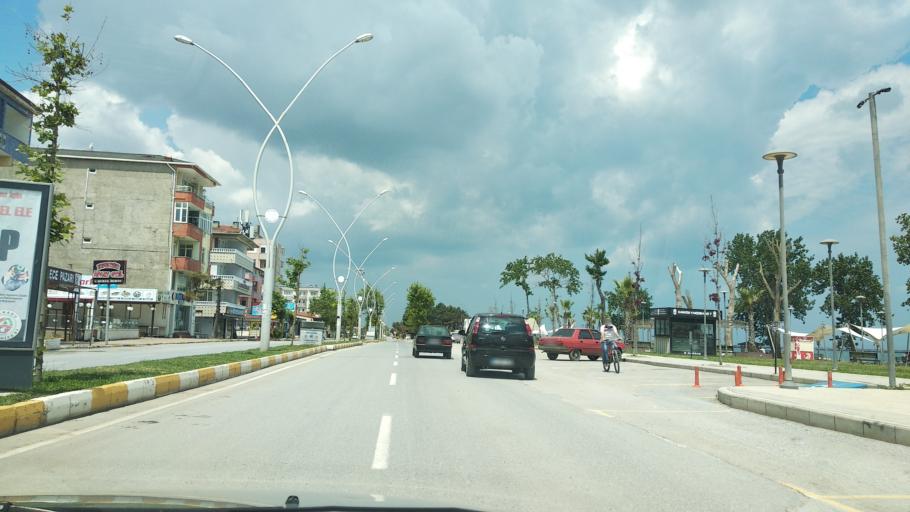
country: TR
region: Sakarya
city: Karasu
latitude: 41.1104
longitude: 30.6923
